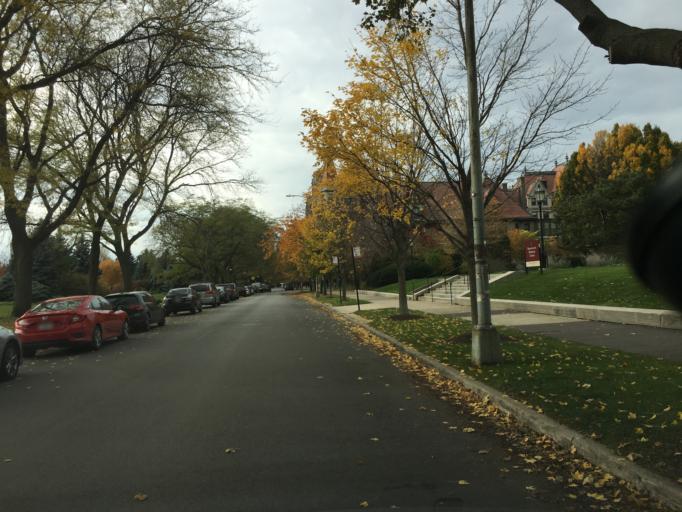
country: US
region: Illinois
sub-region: Cook County
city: Chicago
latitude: 41.7878
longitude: -87.5966
